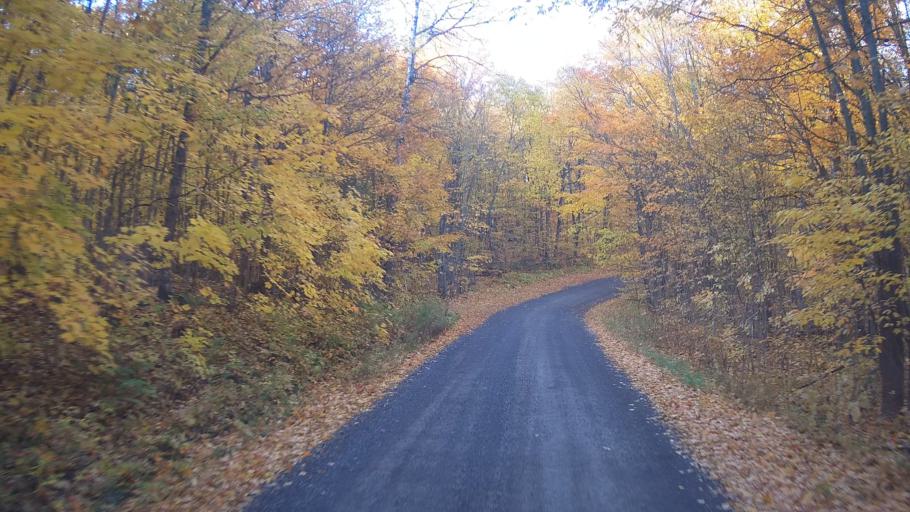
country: CA
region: Ontario
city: Arnprior
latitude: 45.3409
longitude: -76.3484
